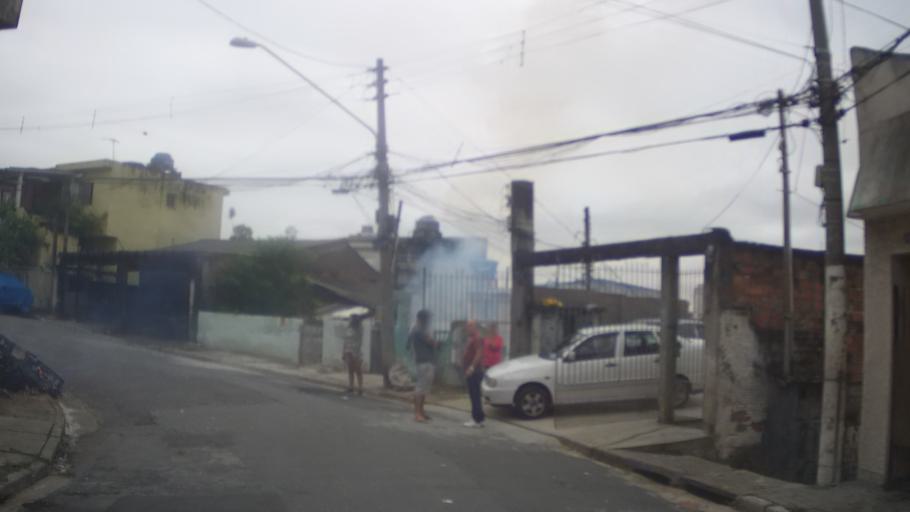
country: BR
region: Sao Paulo
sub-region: Guarulhos
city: Guarulhos
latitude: -23.4508
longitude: -46.5467
